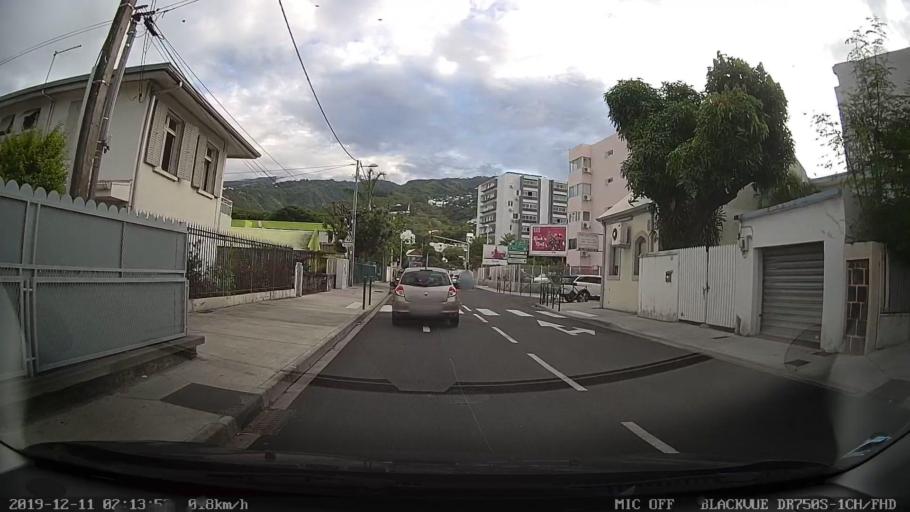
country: RE
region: Reunion
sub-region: Reunion
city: Saint-Denis
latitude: -20.8893
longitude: 55.4532
